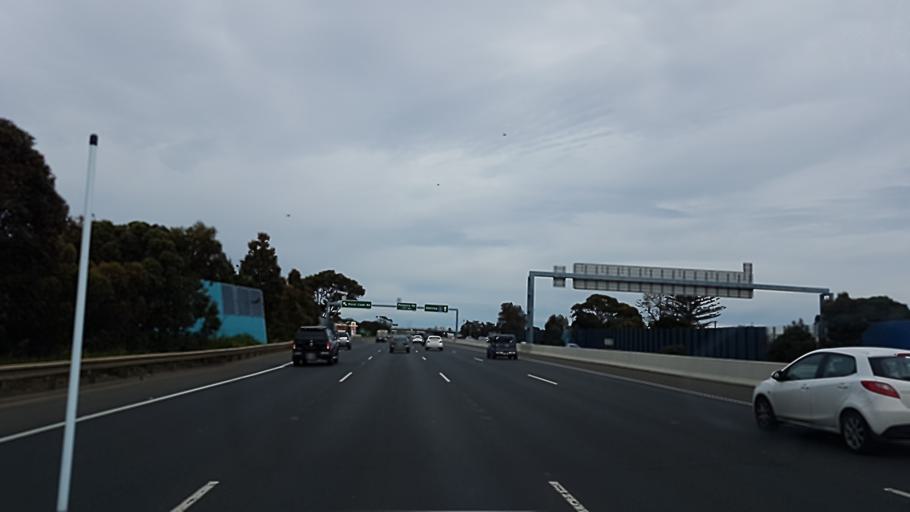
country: AU
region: Victoria
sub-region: Hobsons Bay
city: Laverton
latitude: -37.8685
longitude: 144.7660
